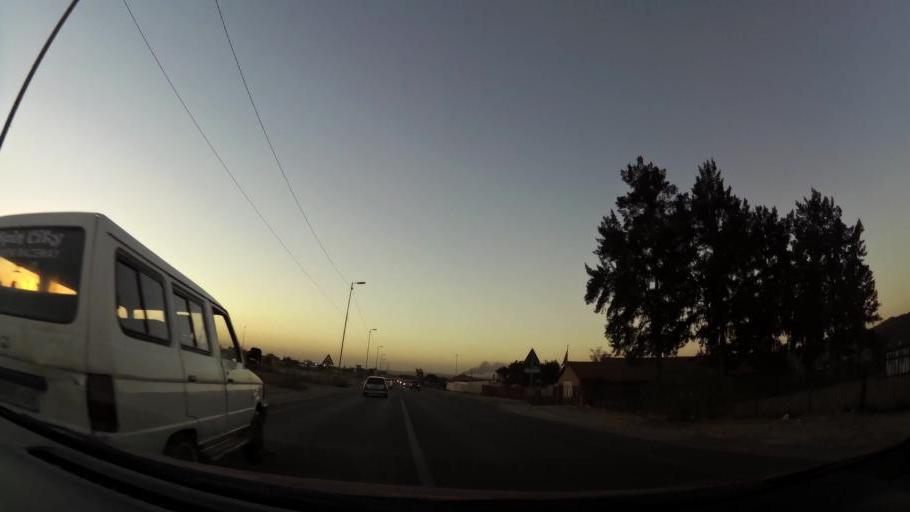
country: ZA
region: North-West
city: Ga-Rankuwa
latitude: -25.6124
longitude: 28.0061
